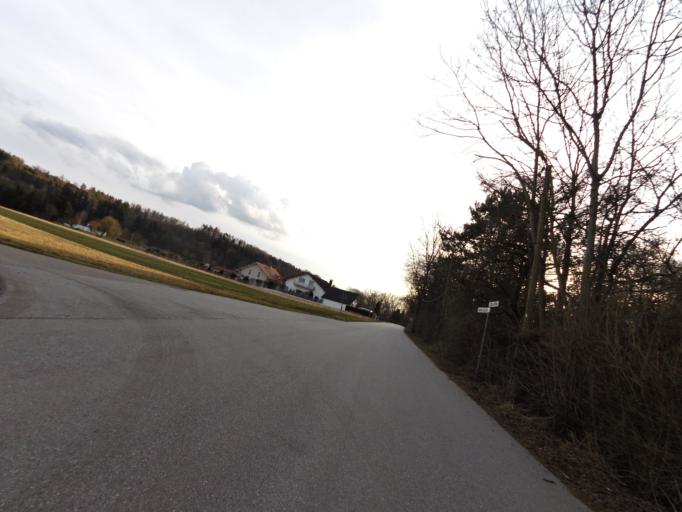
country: DE
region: Bavaria
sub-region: Lower Bavaria
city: Eching
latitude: 48.5007
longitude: 12.0478
